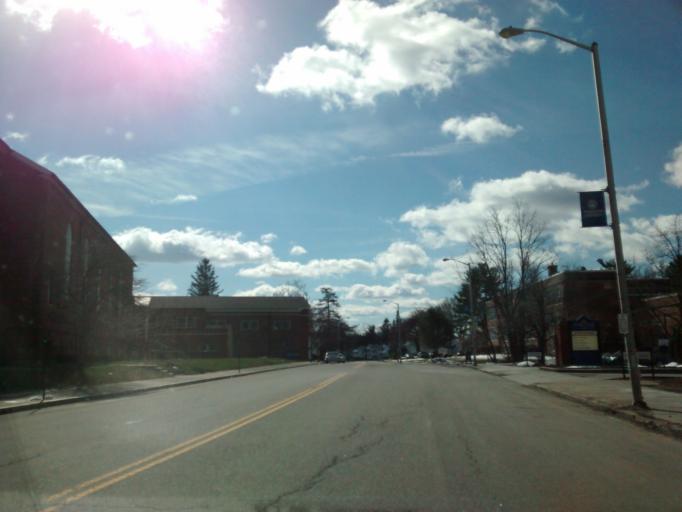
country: US
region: Massachusetts
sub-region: Worcester County
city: Worcester
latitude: 42.2674
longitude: -71.8407
